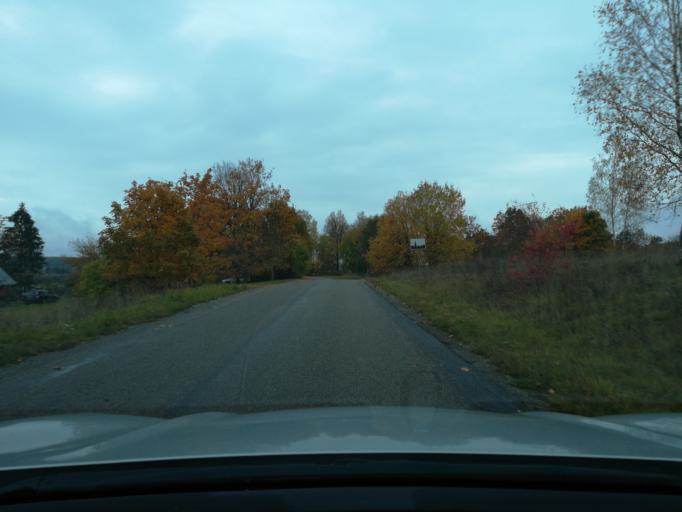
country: EE
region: Ida-Virumaa
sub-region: Johvi vald
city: Johvi
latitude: 59.1914
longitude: 27.5503
